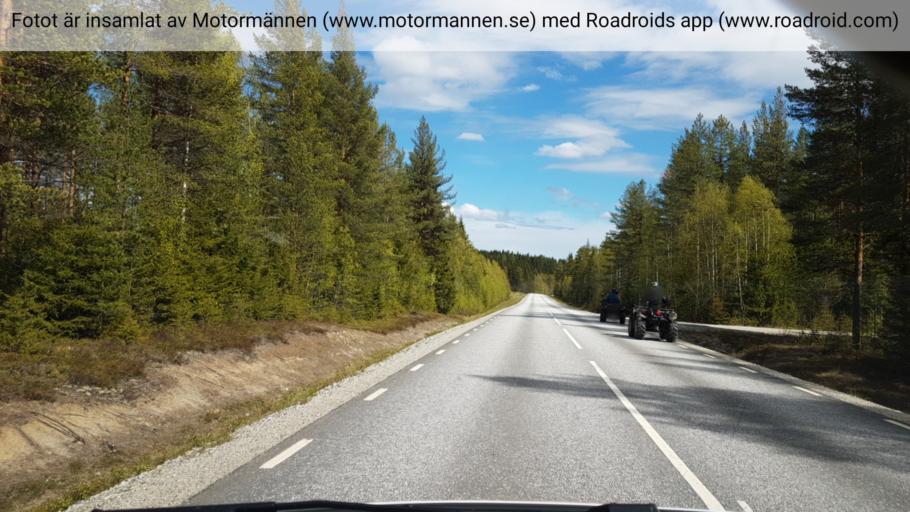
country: SE
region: Vaesterbotten
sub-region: Vindelns Kommun
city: Vindeln
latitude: 64.2087
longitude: 19.6602
